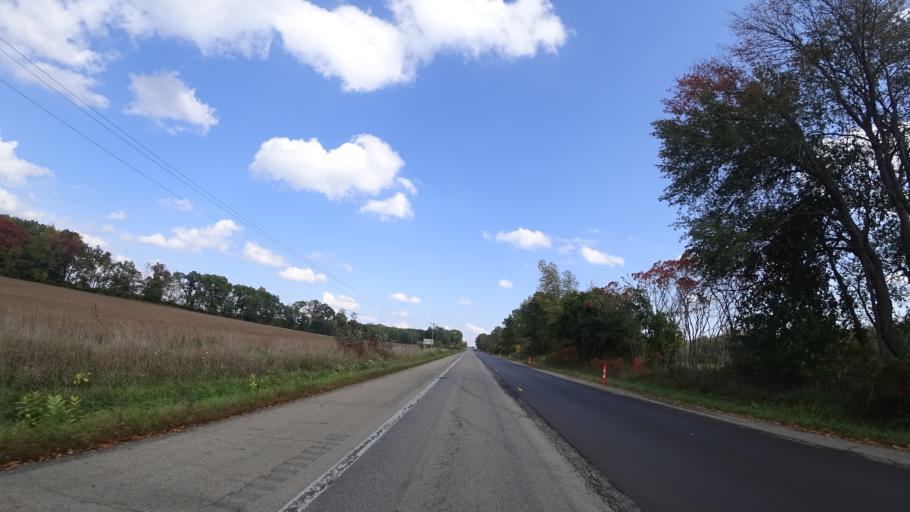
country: US
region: Michigan
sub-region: Branch County
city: Union City
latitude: 42.1075
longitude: -84.9828
